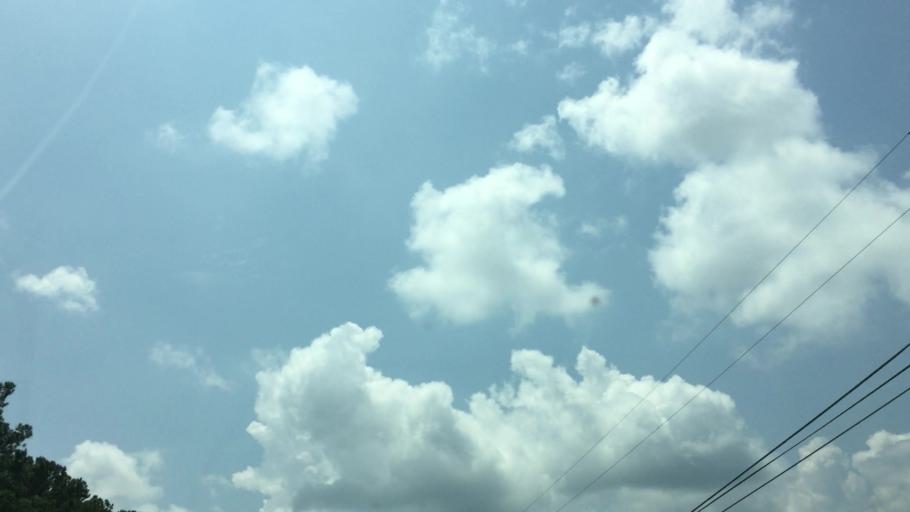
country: US
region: Georgia
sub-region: Carroll County
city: Villa Rica
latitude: 33.6163
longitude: -84.9563
